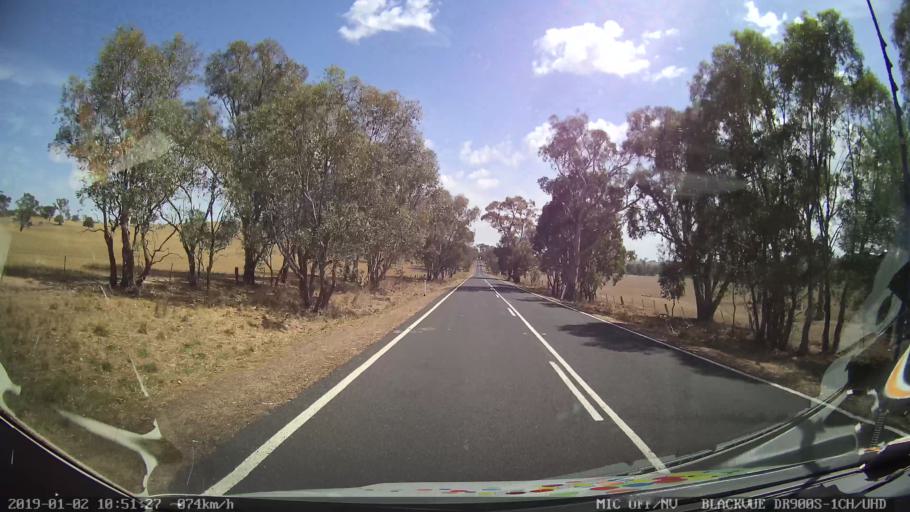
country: AU
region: New South Wales
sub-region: Cootamundra
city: Cootamundra
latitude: -34.7000
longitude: 148.2758
